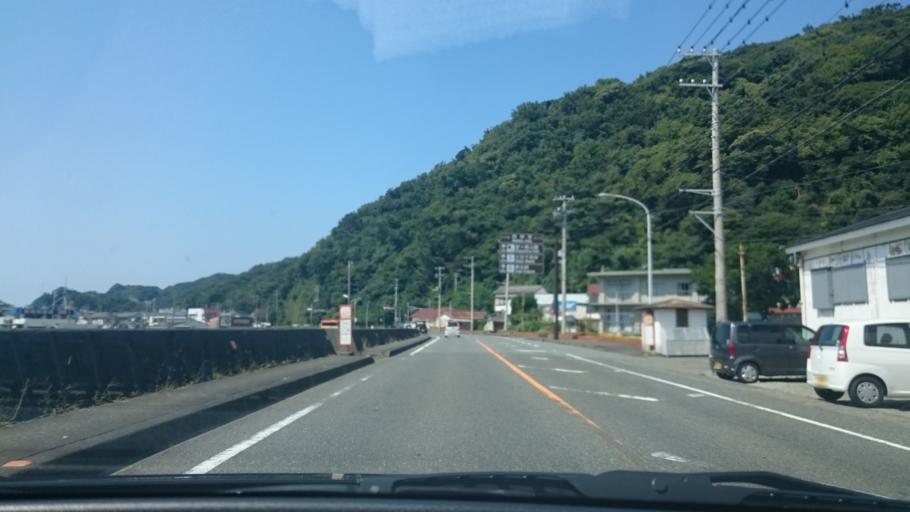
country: JP
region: Shizuoka
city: Heda
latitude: 34.7731
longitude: 138.7713
